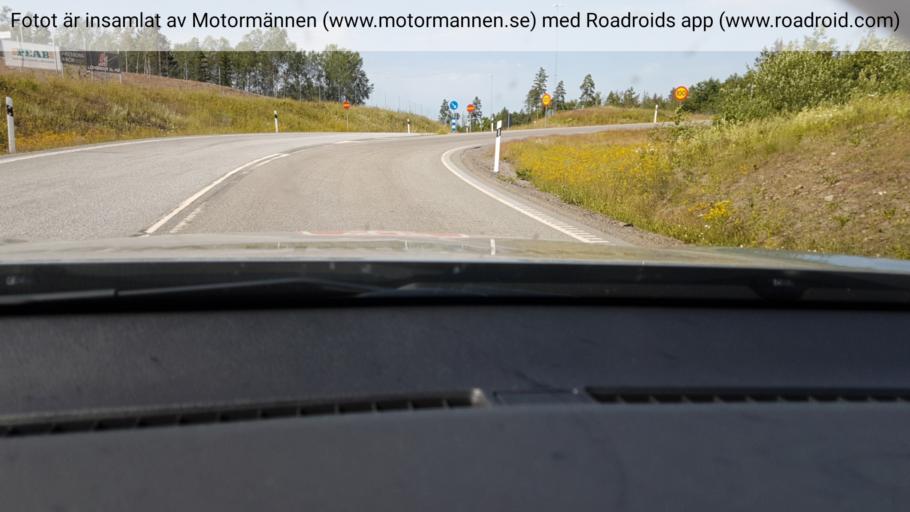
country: SE
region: Joenkoeping
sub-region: Tranas Kommun
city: Tranas
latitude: 58.0338
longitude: 14.9496
